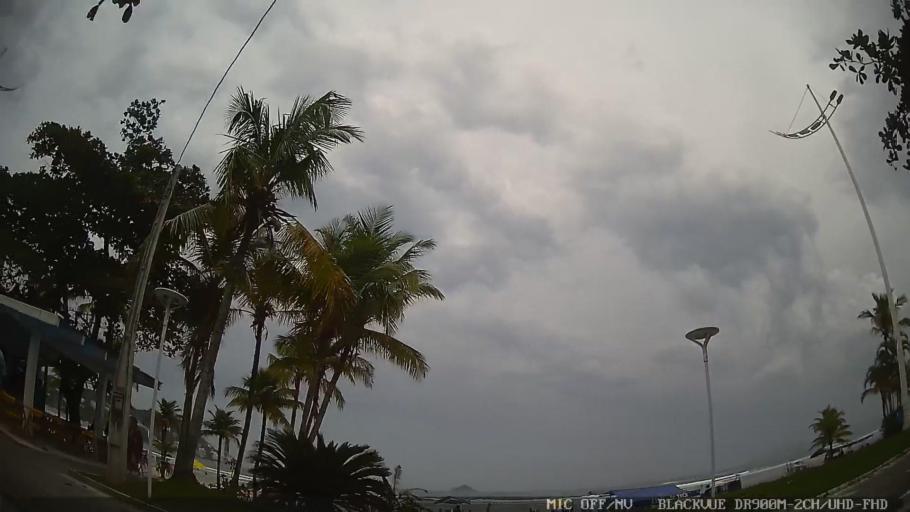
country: BR
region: Sao Paulo
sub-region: Guaruja
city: Guaruja
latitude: -23.9853
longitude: -46.2099
